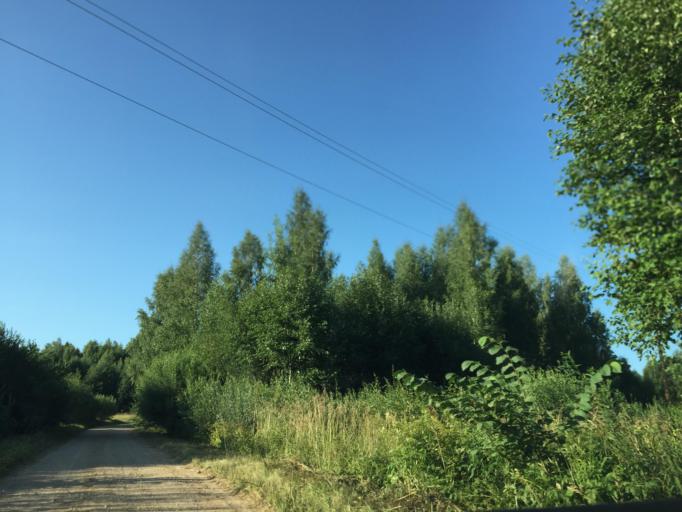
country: LV
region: Kandava
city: Kandava
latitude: 57.0149
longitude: 22.7438
